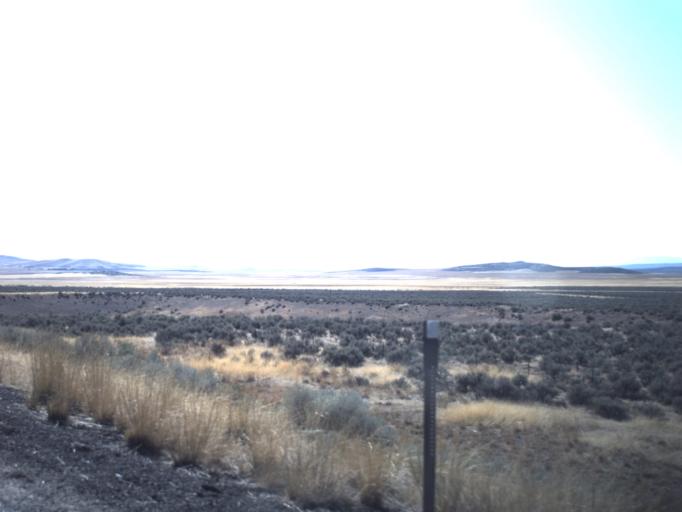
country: US
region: Utah
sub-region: Millard County
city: Fillmore
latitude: 39.0839
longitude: -112.2783
